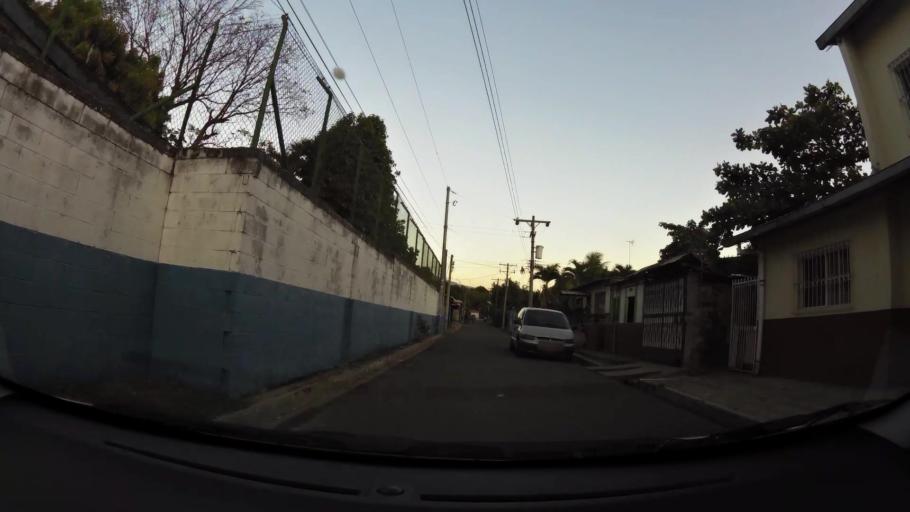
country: SV
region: Sonsonate
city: Armenia
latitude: 13.7347
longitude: -89.3844
